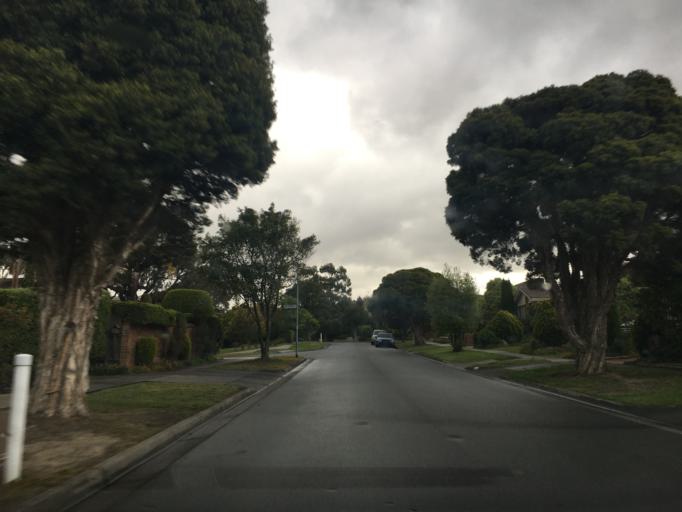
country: AU
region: Victoria
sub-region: Whitehorse
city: Vermont South
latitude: -37.8851
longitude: 145.1865
